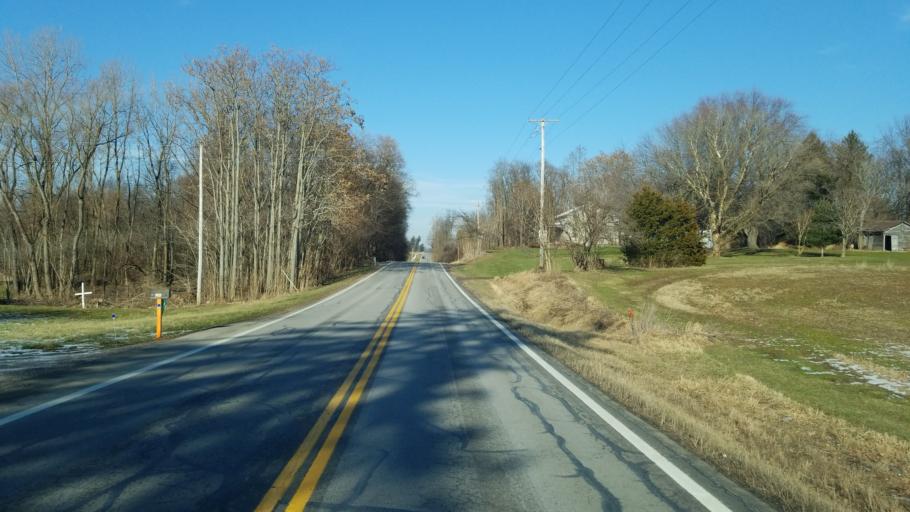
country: US
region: Ohio
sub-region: Huron County
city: Willard
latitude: 41.1101
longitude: -82.6606
